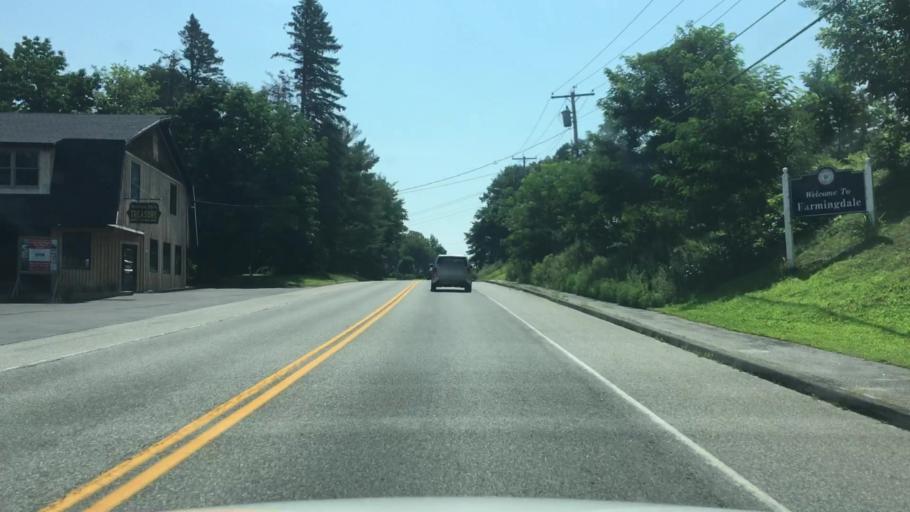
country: US
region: Maine
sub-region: Kennebec County
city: Hallowell
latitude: 44.2667
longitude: -69.7861
